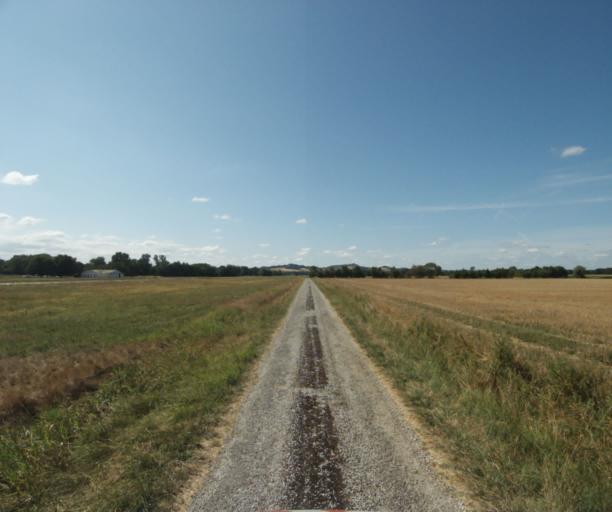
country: FR
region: Midi-Pyrenees
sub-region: Departement de la Haute-Garonne
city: Revel
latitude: 43.4815
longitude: 1.9776
